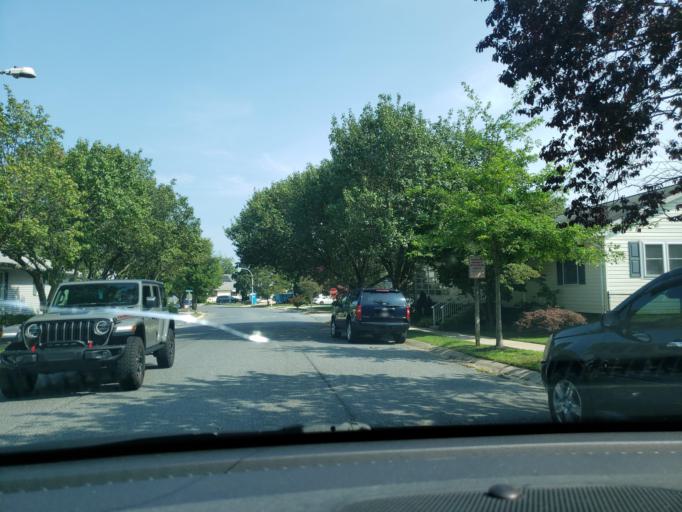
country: US
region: Delaware
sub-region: Sussex County
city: Rehoboth Beach
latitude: 38.7137
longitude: -75.0895
